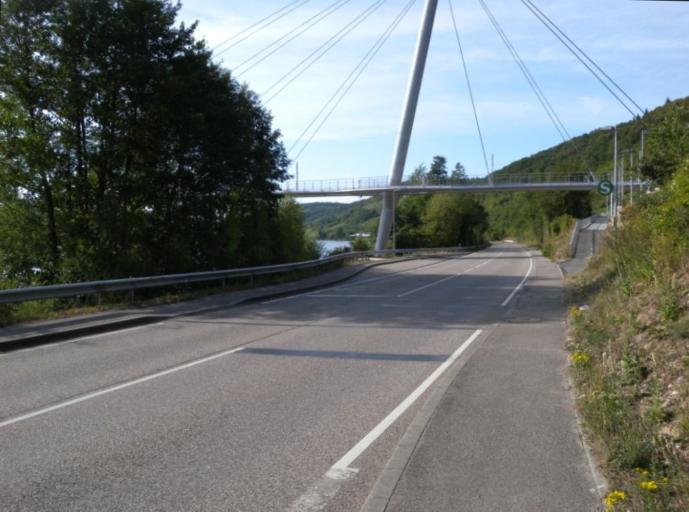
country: DE
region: Baden-Wuerttemberg
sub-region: Karlsruhe Region
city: Hassmersheim
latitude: 49.3032
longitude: 9.1541
